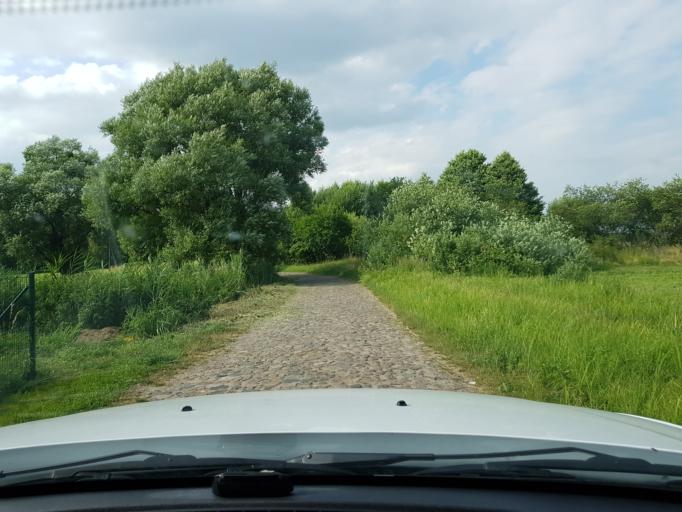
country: PL
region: West Pomeranian Voivodeship
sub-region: Powiat gryfinski
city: Chojna
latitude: 52.9940
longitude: 14.4865
